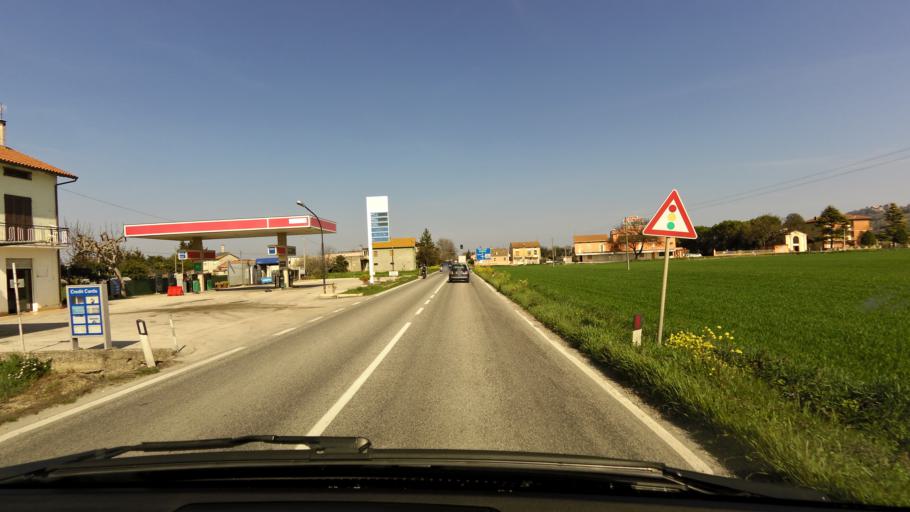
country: IT
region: The Marches
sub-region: Provincia di Macerata
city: Potenza Picena
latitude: 43.3793
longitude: 13.6064
